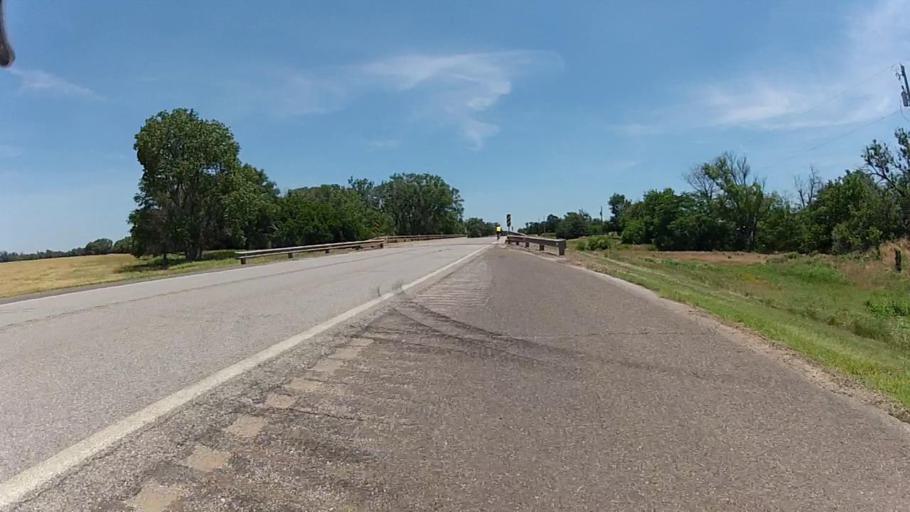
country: US
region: Kansas
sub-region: Barber County
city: Medicine Lodge
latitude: 37.2536
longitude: -98.4122
